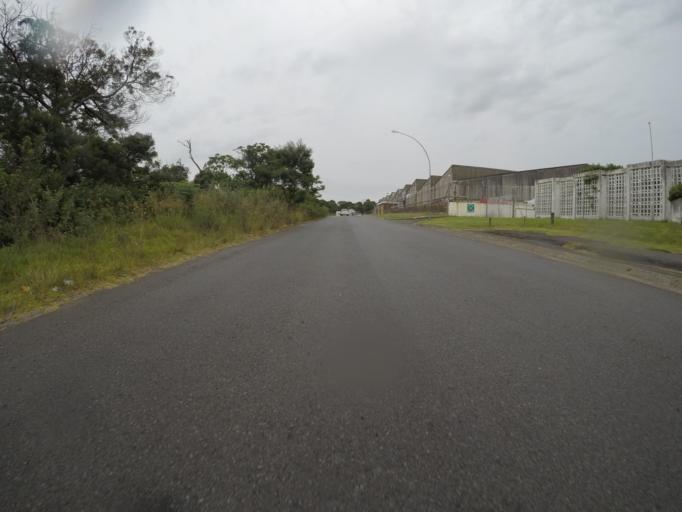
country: ZA
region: Eastern Cape
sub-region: Buffalo City Metropolitan Municipality
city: East London
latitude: -32.9703
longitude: 27.8189
